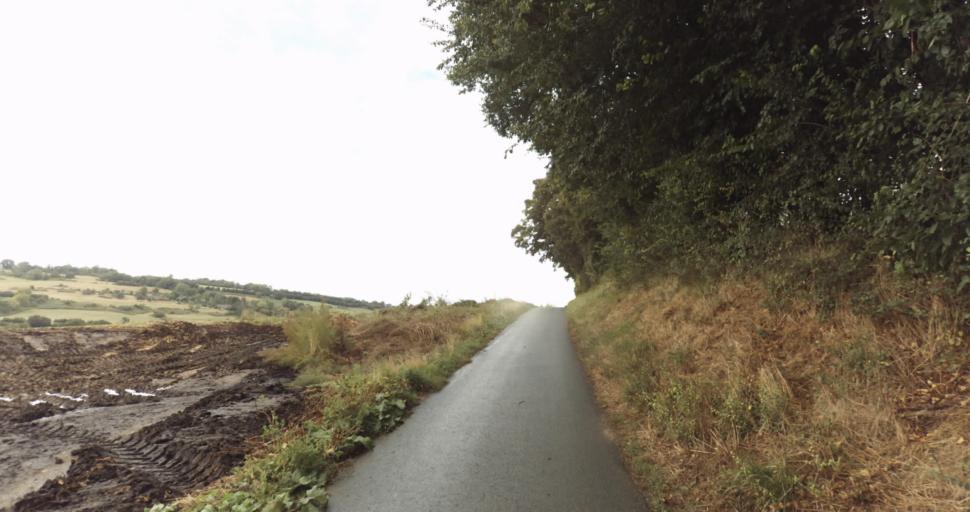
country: FR
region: Lower Normandy
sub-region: Departement de l'Orne
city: Vimoutiers
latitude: 48.8598
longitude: 0.2314
